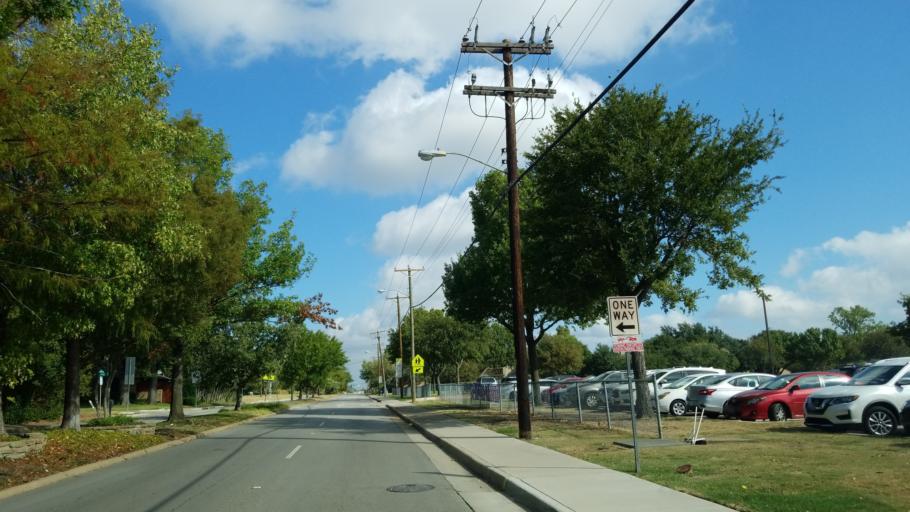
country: US
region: Texas
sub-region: Dallas County
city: Richardson
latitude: 32.9470
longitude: -96.7786
